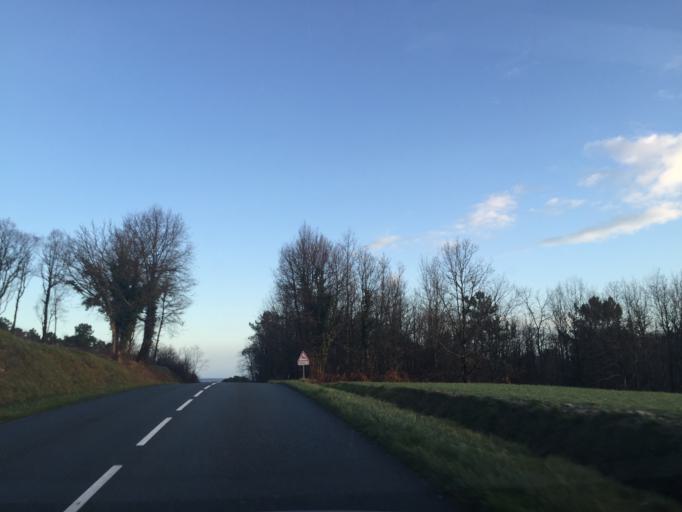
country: FR
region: Poitou-Charentes
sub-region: Departement de la Charente
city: Chalais
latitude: 45.2736
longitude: 0.0888
